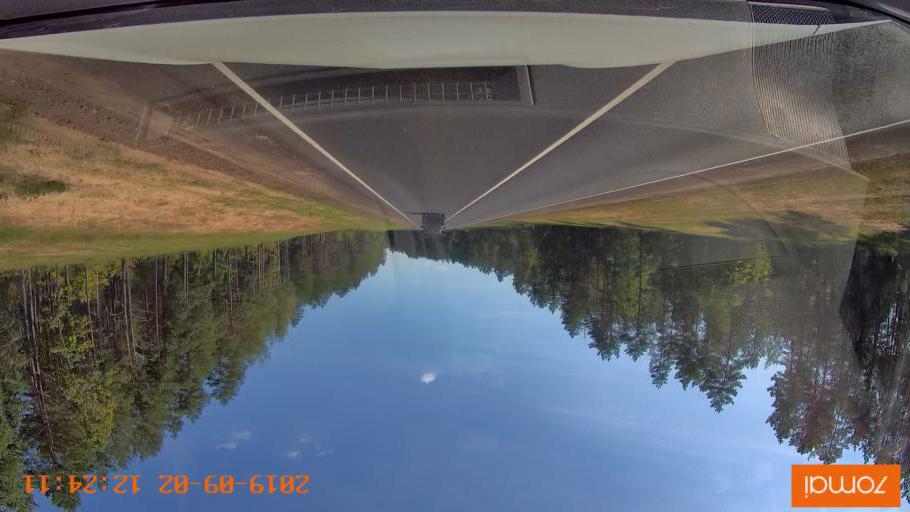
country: RU
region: Smolensk
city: Shumyachi
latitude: 53.8703
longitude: 32.6123
